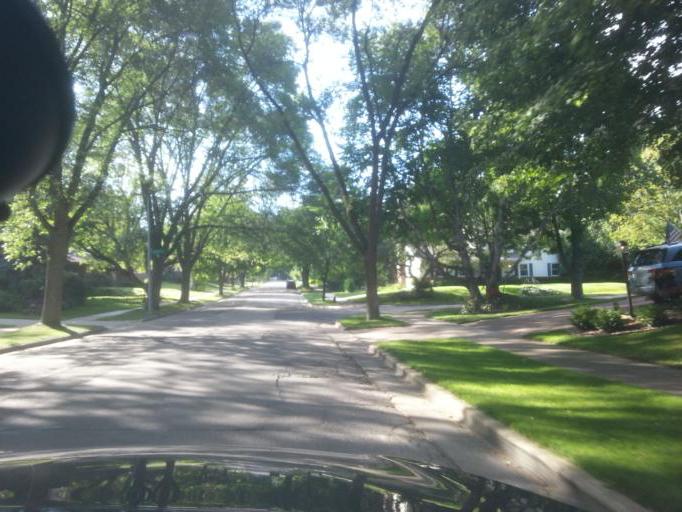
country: US
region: Wisconsin
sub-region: Dane County
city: Middleton
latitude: 43.0705
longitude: -89.4941
